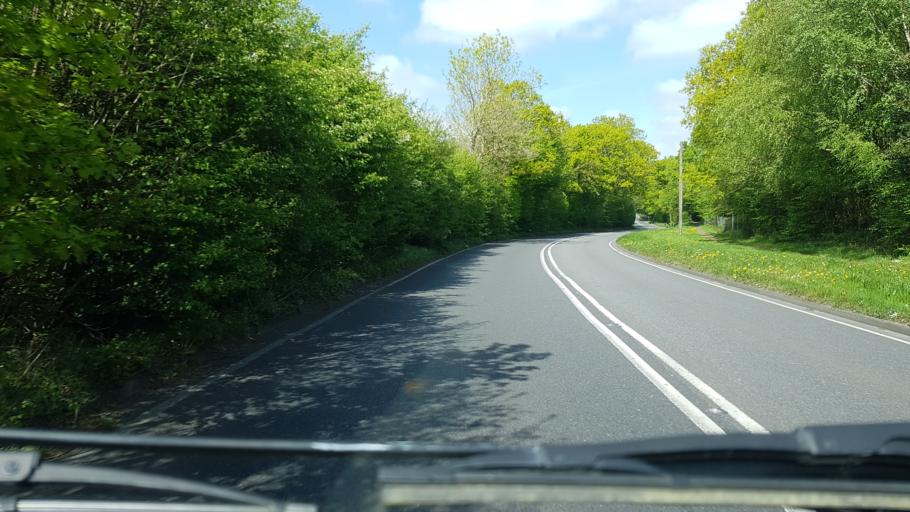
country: GB
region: England
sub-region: Kent
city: Hawkhurst
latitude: 51.0456
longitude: 0.4464
